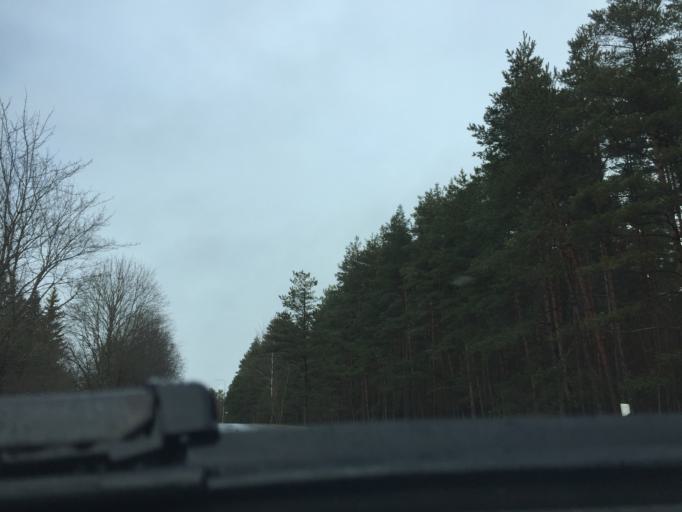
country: EE
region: Laeaene
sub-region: Haapsalu linn
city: Haapsalu
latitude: 58.9179
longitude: 23.5496
